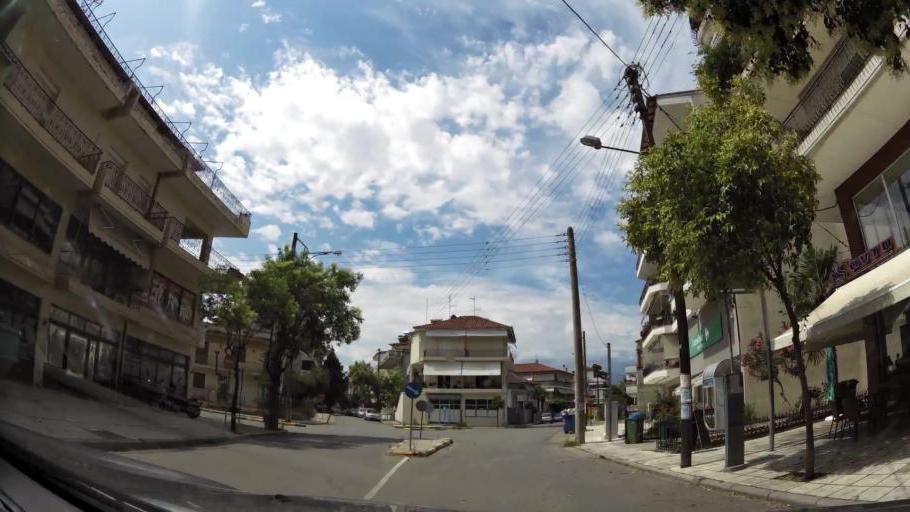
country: GR
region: Central Macedonia
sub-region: Nomos Pierias
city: Katerini
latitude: 40.2742
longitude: 22.4987
